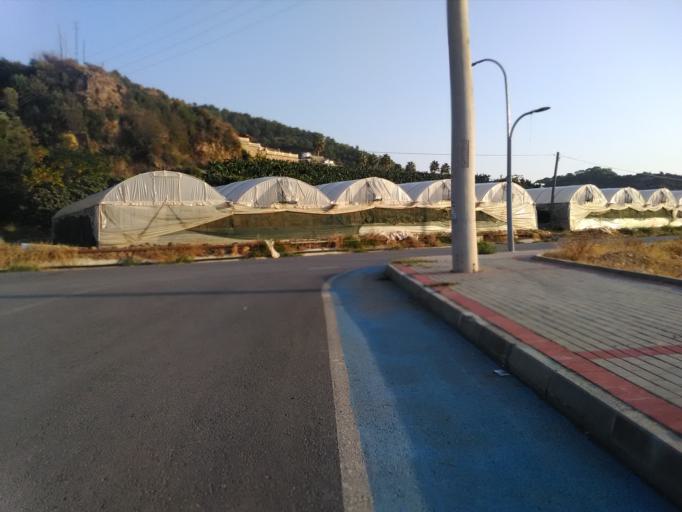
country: TR
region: Antalya
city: Gazipasa
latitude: 36.2410
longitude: 32.2997
